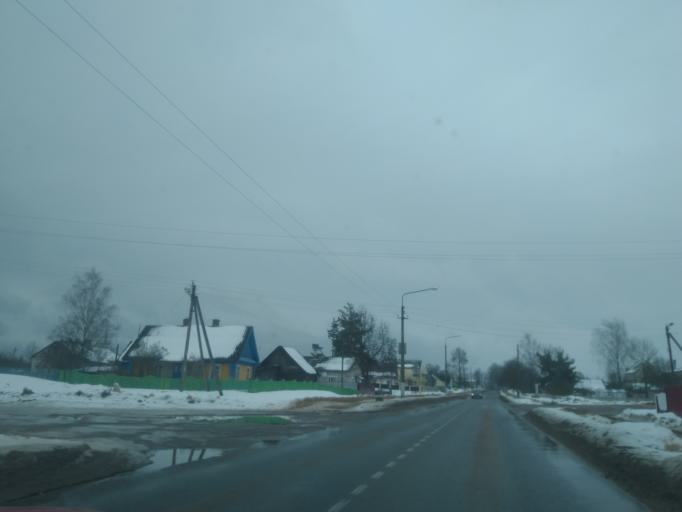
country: BY
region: Minsk
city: Ivyanyets
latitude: 53.8964
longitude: 26.7461
